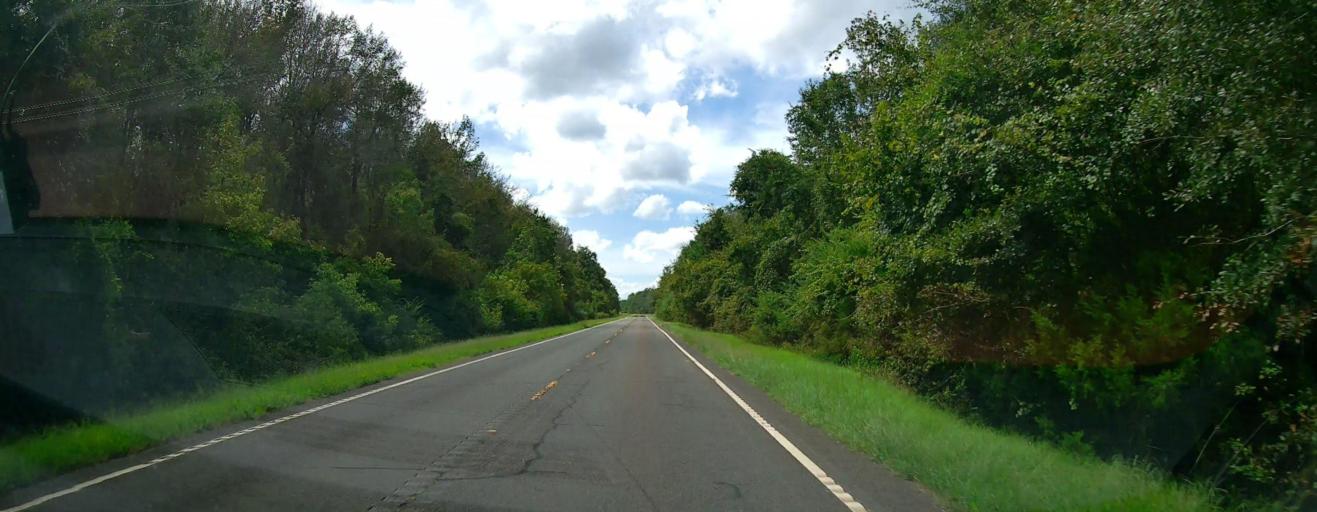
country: US
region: Georgia
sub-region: Macon County
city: Marshallville
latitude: 32.4335
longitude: -84.0387
